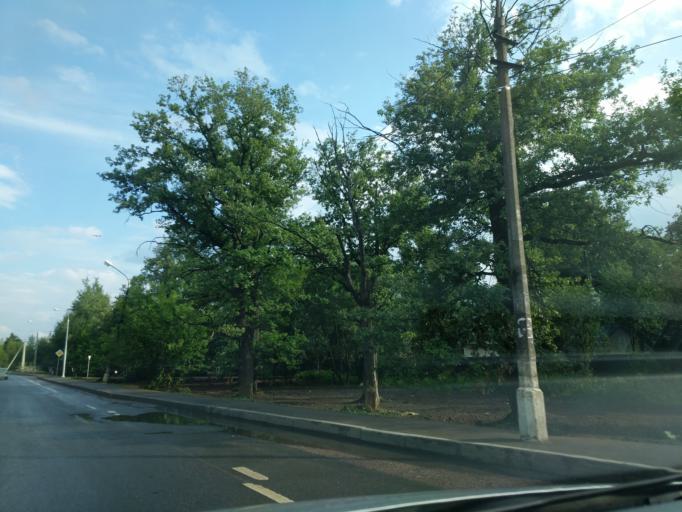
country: RU
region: Moskovskaya
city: Lobnya
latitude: 56.0102
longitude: 37.5070
